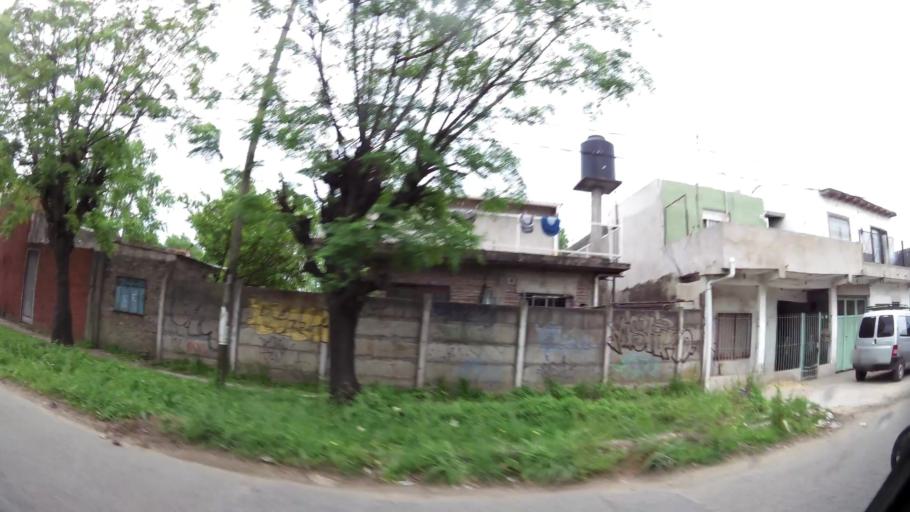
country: AR
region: Buenos Aires
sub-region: Partido de Quilmes
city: Quilmes
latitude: -34.7977
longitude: -58.2698
